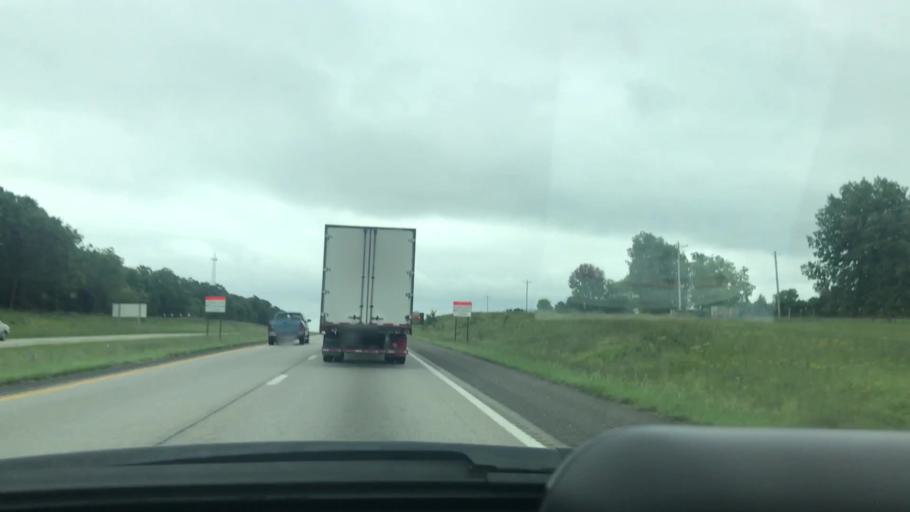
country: US
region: Missouri
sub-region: Greene County
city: Republic
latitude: 37.1858
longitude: -93.5581
